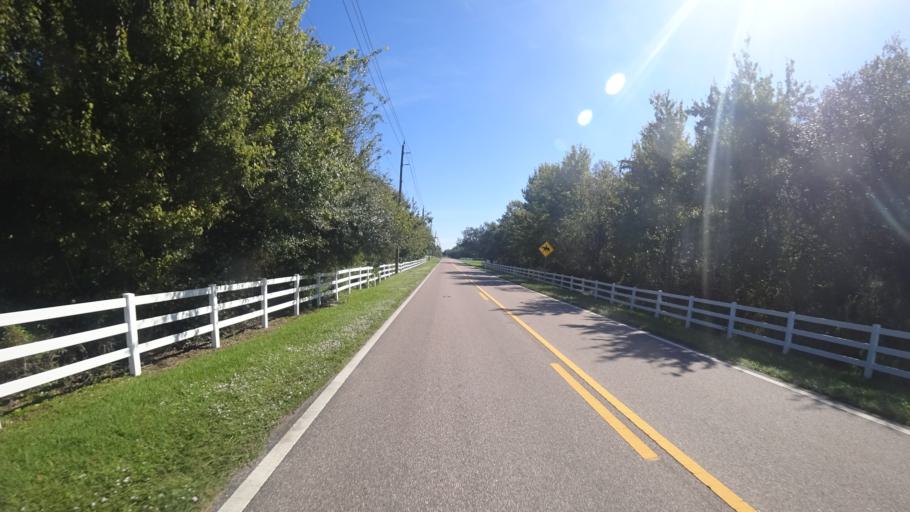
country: US
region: Florida
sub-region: Sarasota County
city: Lake Sarasota
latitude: 27.3500
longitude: -82.2623
